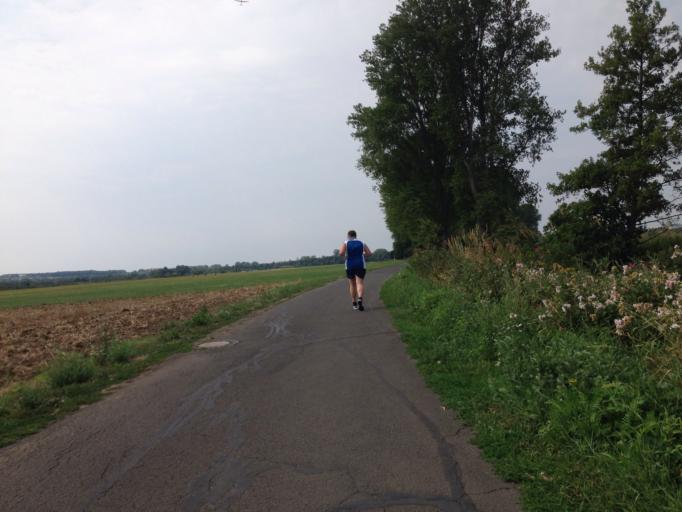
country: DE
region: Hesse
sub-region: Regierungsbezirk Giessen
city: Alten Buseck
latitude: 50.6055
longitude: 8.7365
